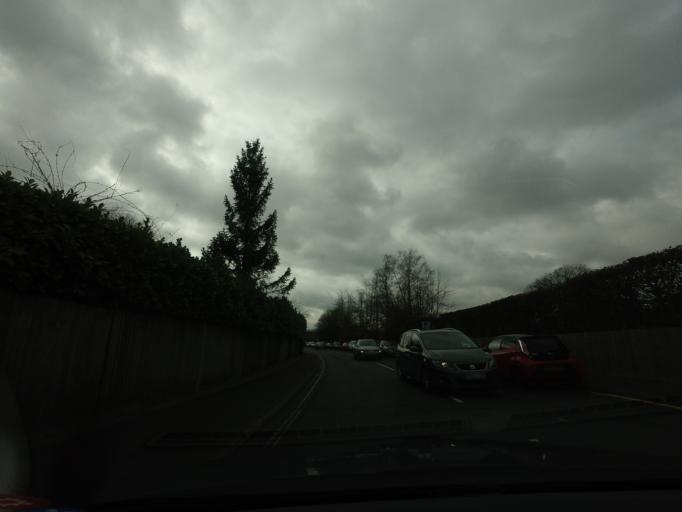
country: GB
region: England
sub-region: Kent
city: Shoreham
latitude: 51.3123
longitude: 0.1902
